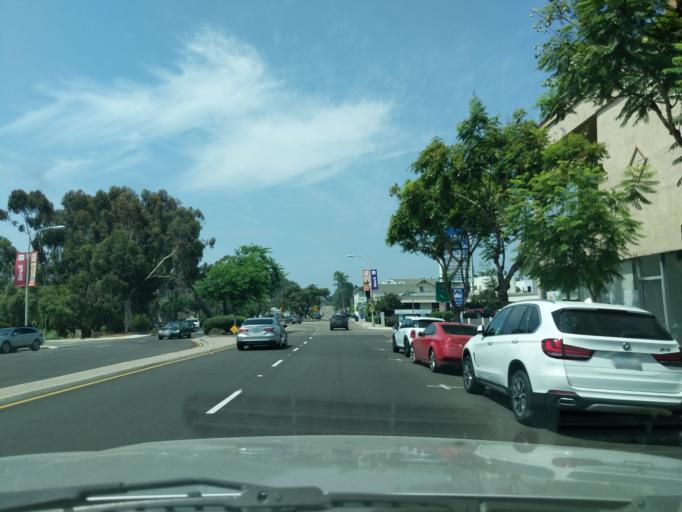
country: US
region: California
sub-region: San Diego County
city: San Diego
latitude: 32.7499
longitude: -117.1718
